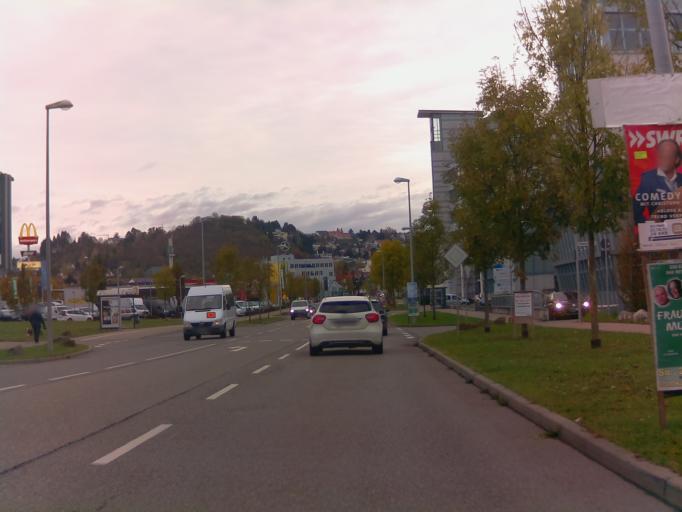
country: DE
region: Baden-Wuerttemberg
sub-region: Regierungsbezirk Stuttgart
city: Leonberg
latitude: 48.7831
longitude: 9.0160
